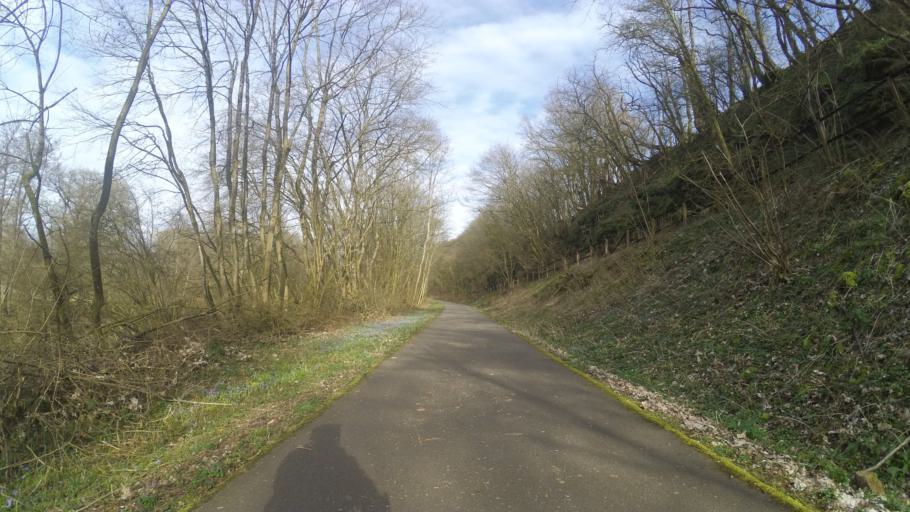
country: DE
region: Saarland
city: Gersheim
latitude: 49.1388
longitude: 7.2023
